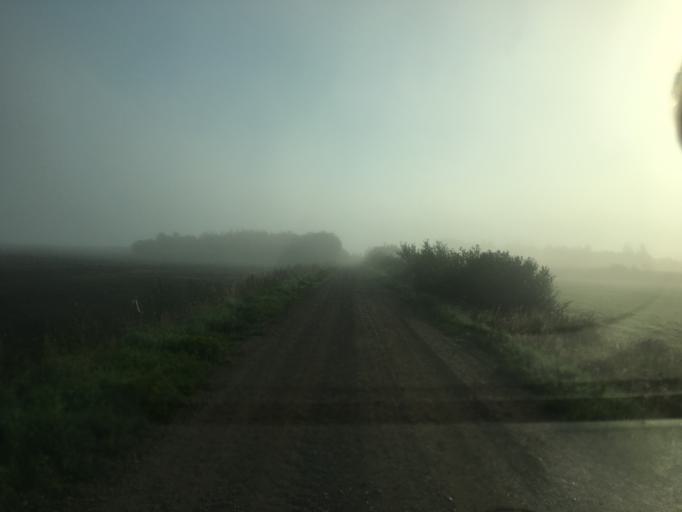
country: DK
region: South Denmark
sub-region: Tonder Kommune
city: Logumkloster
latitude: 55.0131
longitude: 8.8961
